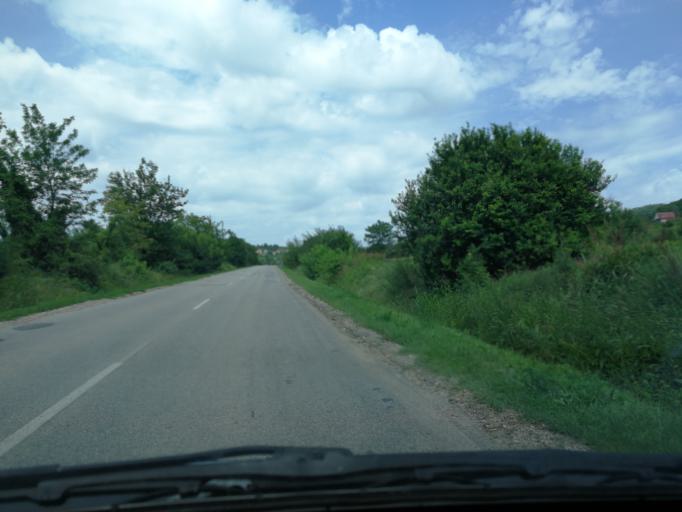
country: HU
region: Baranya
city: Harkany
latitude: 45.8776
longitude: 18.2429
